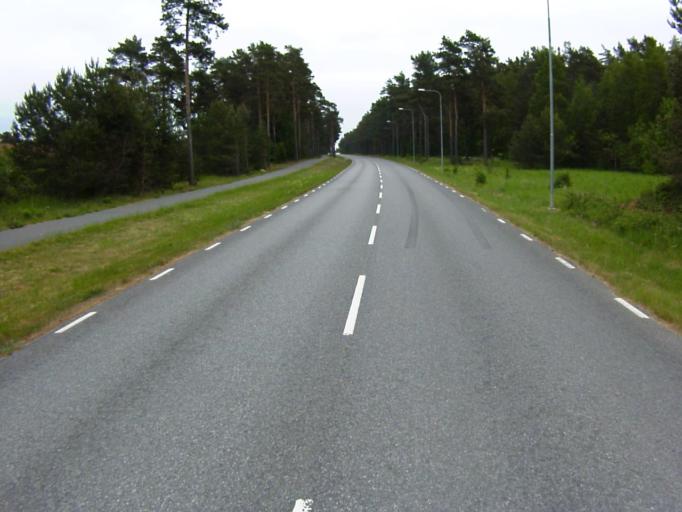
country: SE
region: Skane
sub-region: Kristianstads Kommun
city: Ahus
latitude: 55.9358
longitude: 14.2700
